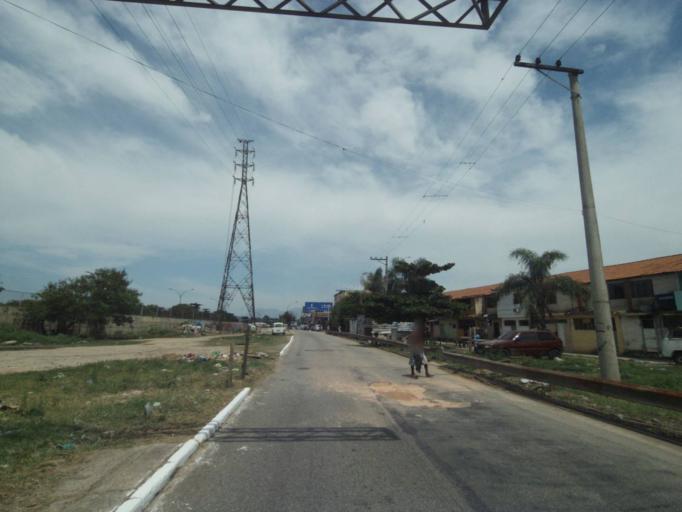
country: BR
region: Rio de Janeiro
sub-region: Duque De Caxias
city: Duque de Caxias
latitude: -22.7983
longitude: -43.3080
